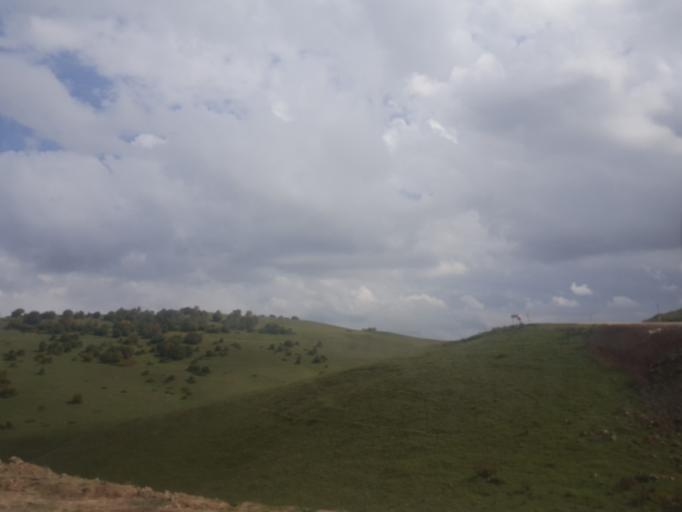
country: TR
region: Tokat
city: Bereketli
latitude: 40.5754
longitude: 37.3030
